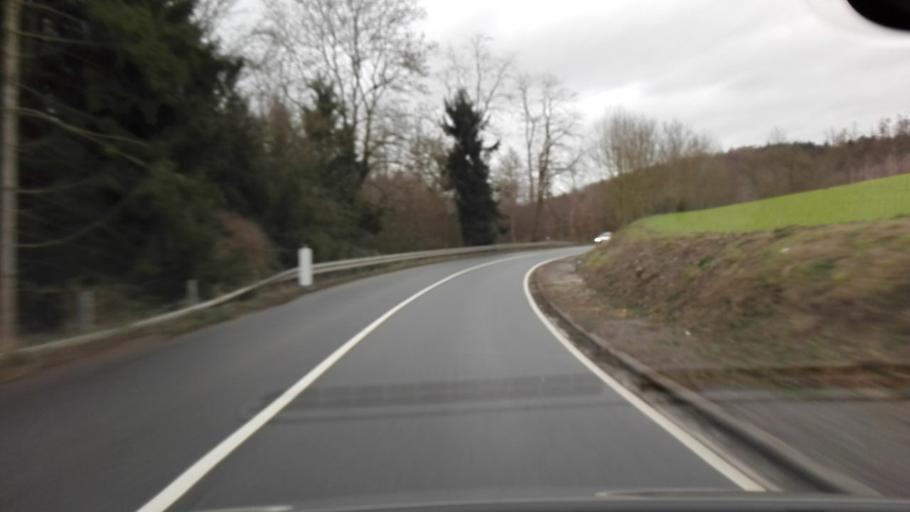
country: DE
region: North Rhine-Westphalia
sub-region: Regierungsbezirk Arnsberg
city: Frondenberg
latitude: 51.4776
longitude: 7.7380
